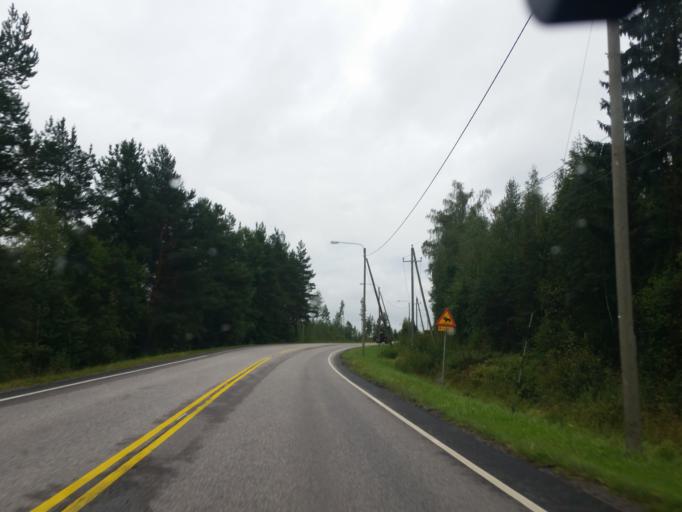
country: FI
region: Uusimaa
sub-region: Helsinki
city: Vihti
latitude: 60.3437
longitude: 24.1944
